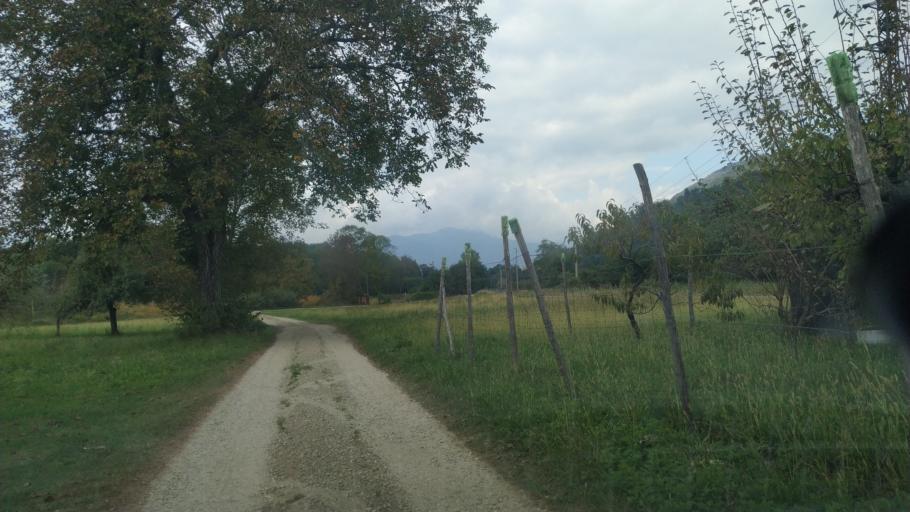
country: IT
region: Piedmont
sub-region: Provincia di Novara
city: Grignasco
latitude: 45.6793
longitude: 8.3340
